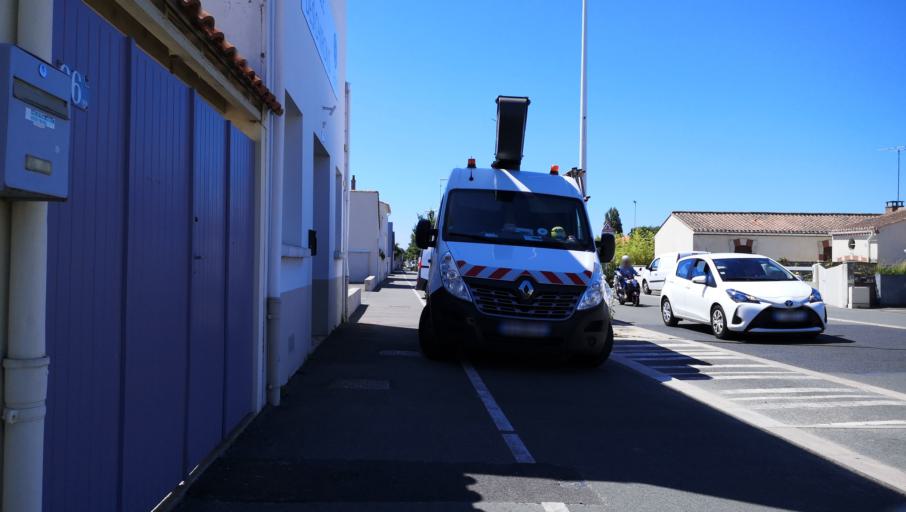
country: FR
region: Pays de la Loire
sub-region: Departement de la Vendee
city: Les Sables-d'Olonne
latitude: 46.5103
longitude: -1.7768
